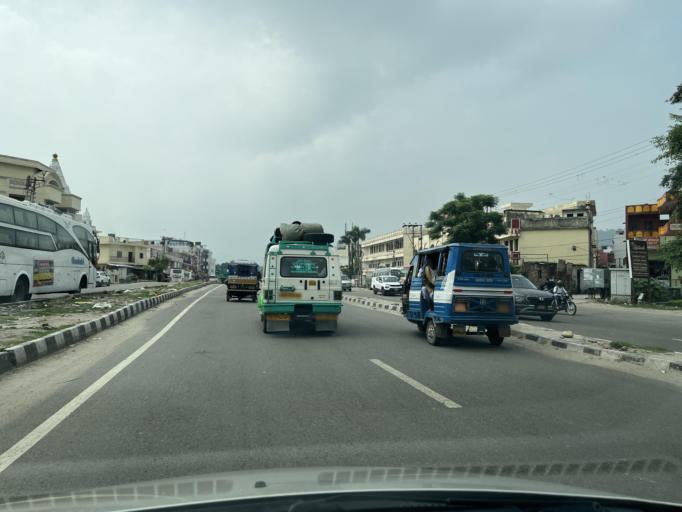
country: IN
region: Uttarakhand
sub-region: Haridwar
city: Haridwar
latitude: 29.9785
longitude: 78.1827
